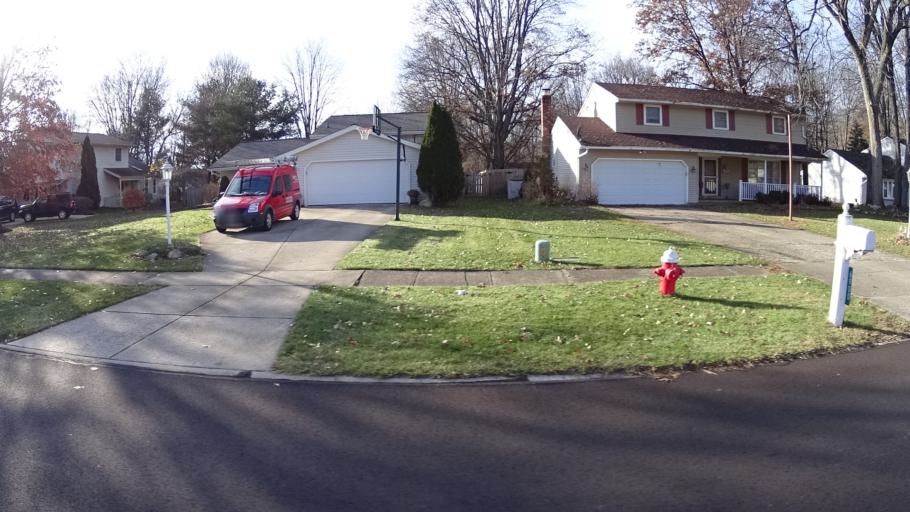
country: US
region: Ohio
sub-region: Lorain County
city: North Ridgeville
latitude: 41.3905
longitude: -81.9976
